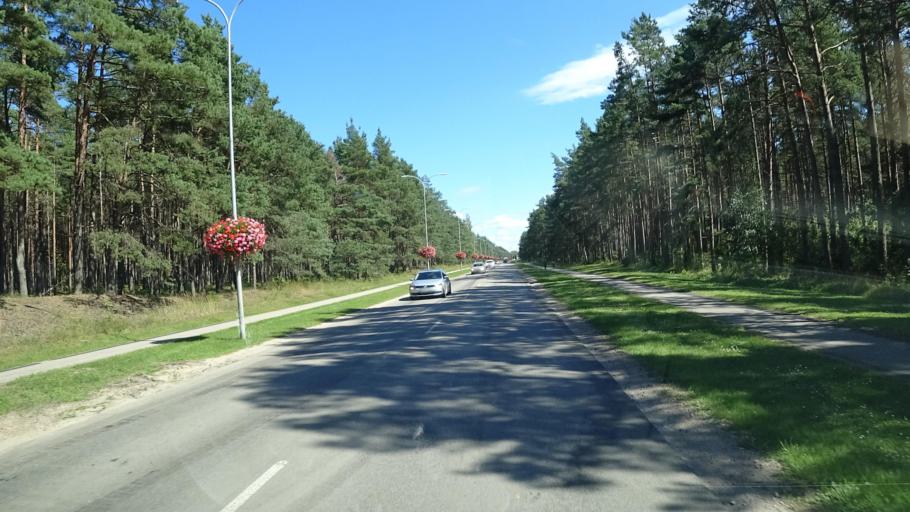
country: LV
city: Tireli
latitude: 56.9663
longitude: 23.5864
